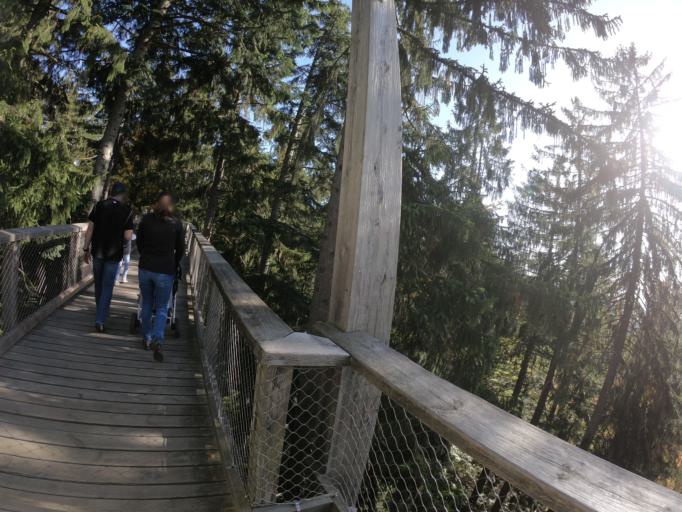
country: DE
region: Bavaria
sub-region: Lower Bavaria
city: Neuschonau
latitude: 48.8910
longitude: 13.4833
